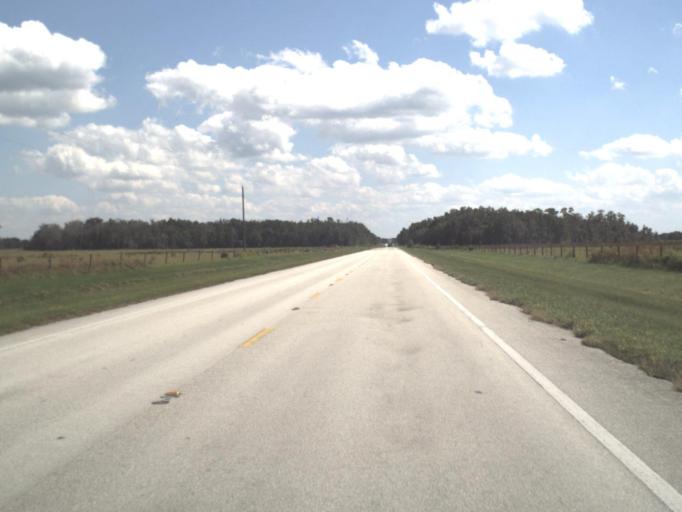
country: US
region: Florida
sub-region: Highlands County
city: Sebring
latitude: 27.4396
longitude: -81.6104
